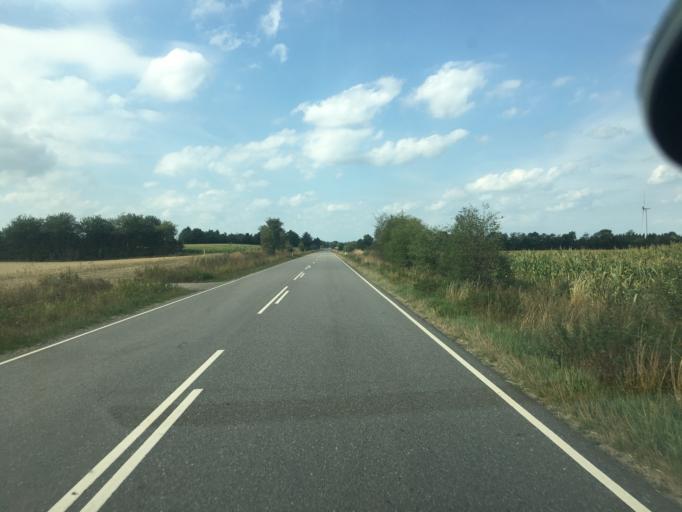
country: DK
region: South Denmark
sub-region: Aabenraa Kommune
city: Tinglev
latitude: 54.9388
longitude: 9.3452
